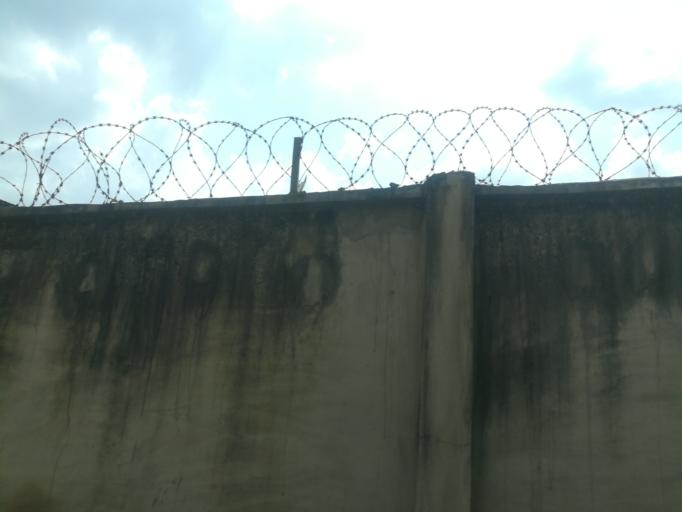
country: NG
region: Oyo
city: Ibadan
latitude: 7.4361
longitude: 3.9358
